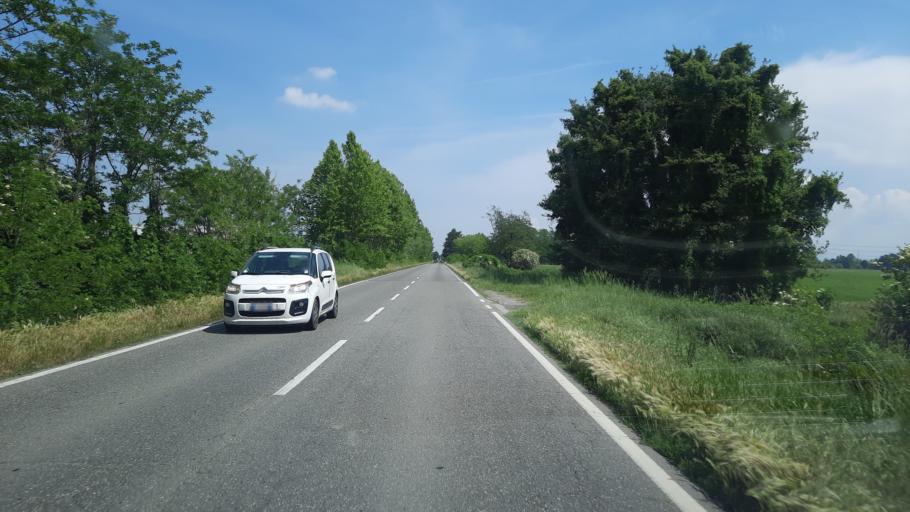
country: IT
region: Lombardy
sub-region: Provincia di Pavia
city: Garlasco
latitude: 45.1891
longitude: 8.9476
